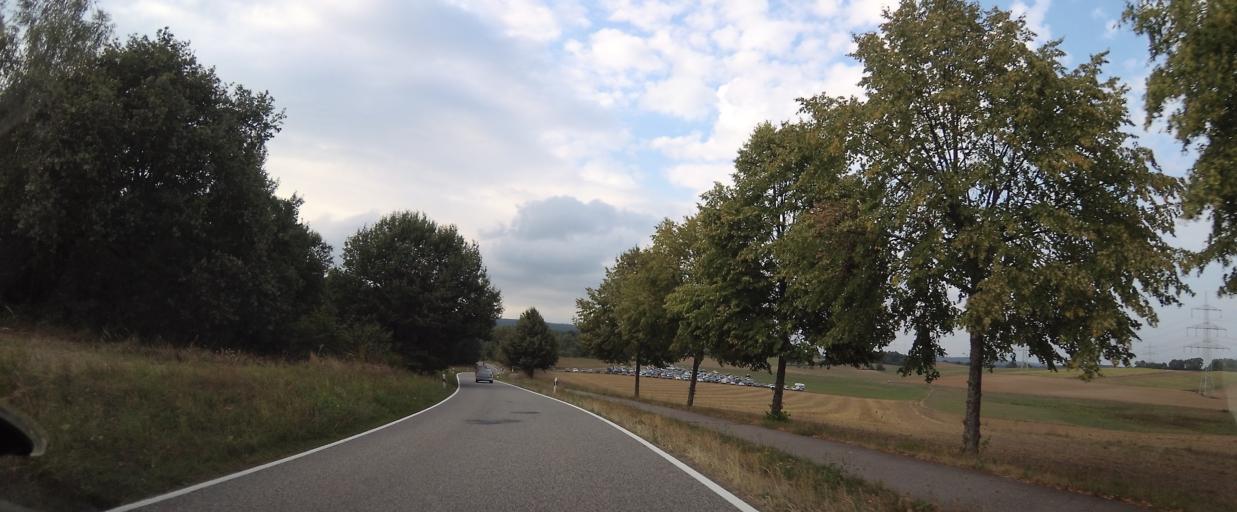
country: DE
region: Saarland
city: Wadern
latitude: 49.5500
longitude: 6.8701
